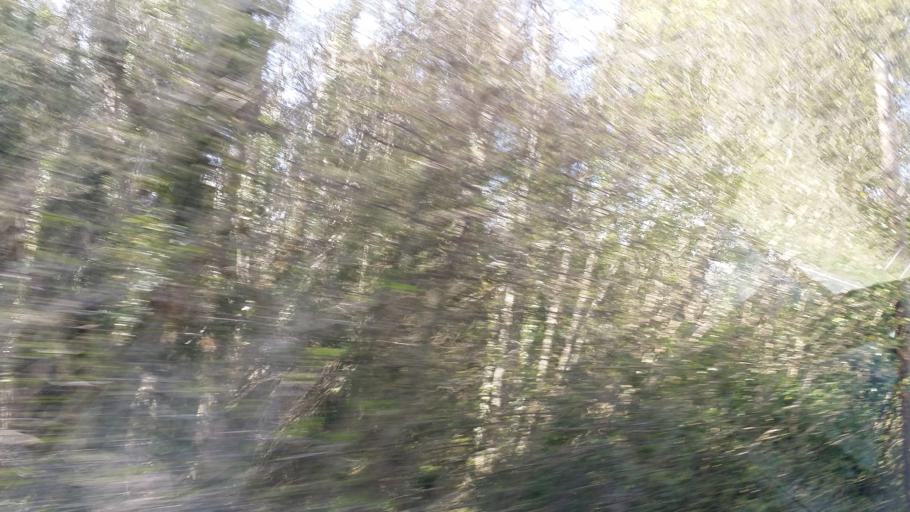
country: GB
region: Northern Ireland
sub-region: Fermanagh District
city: Enniskillen
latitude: 54.3999
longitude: -7.7167
